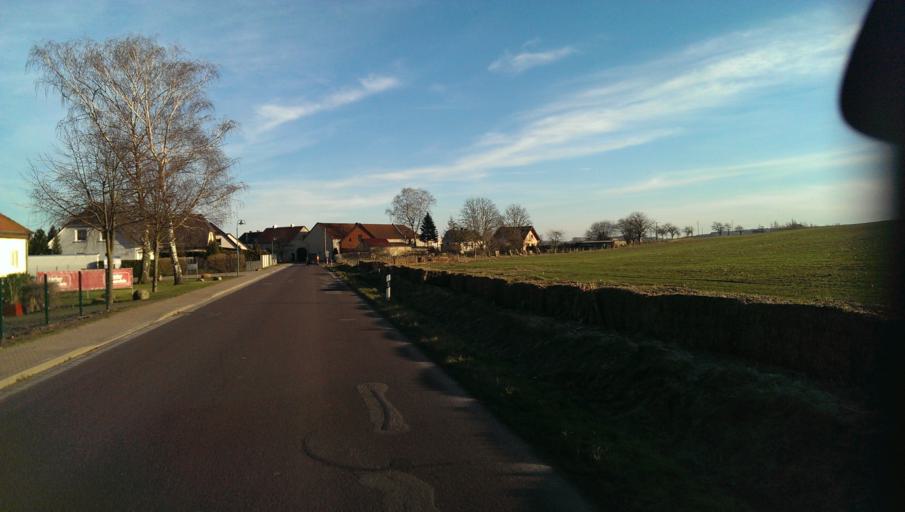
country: DE
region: Saxony-Anhalt
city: Eilsleben
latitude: 52.1308
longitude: 11.1935
